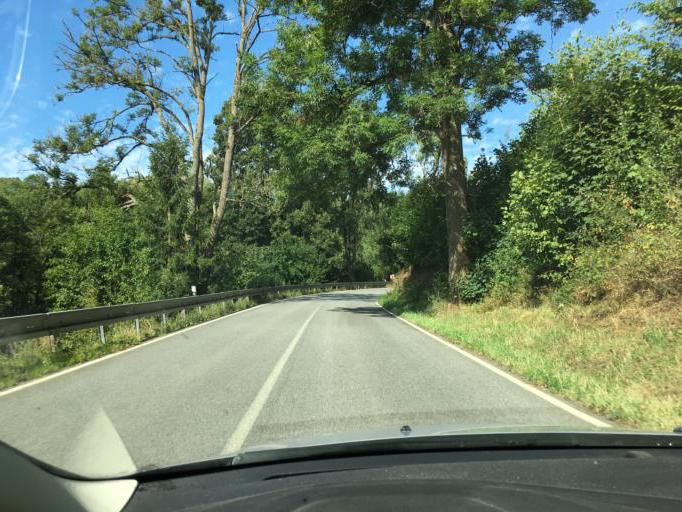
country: CZ
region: Liberecky
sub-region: Okres Semily
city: Ponikla
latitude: 50.6434
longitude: 15.4370
